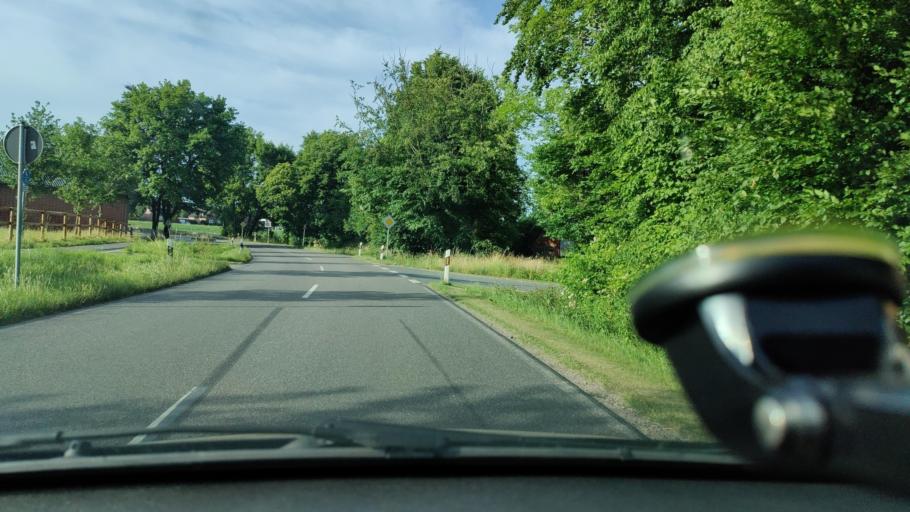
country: DE
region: North Rhine-Westphalia
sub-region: Regierungsbezirk Munster
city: Coesfeld
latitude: 52.0089
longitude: 7.1911
